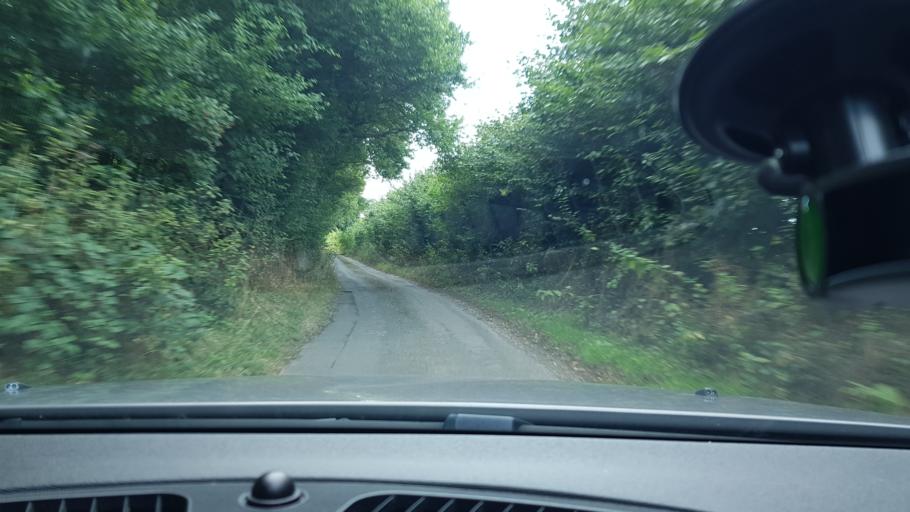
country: GB
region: England
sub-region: West Berkshire
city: Hungerford
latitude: 51.4202
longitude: -1.4915
